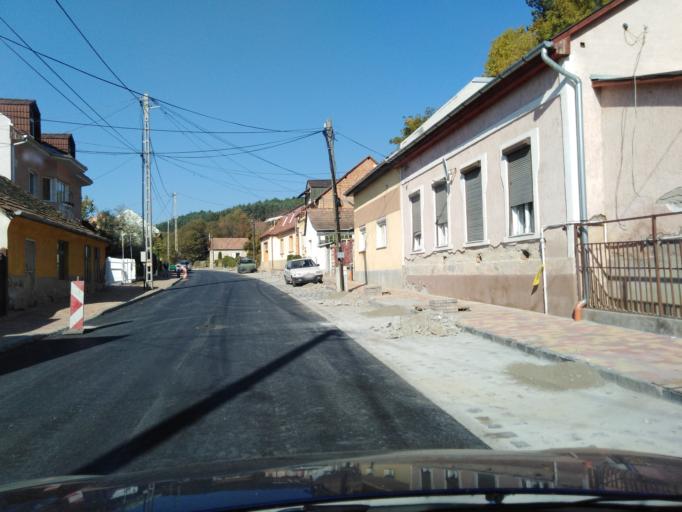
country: HU
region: Nograd
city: Salgotarjan
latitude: 48.1058
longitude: 19.8006
